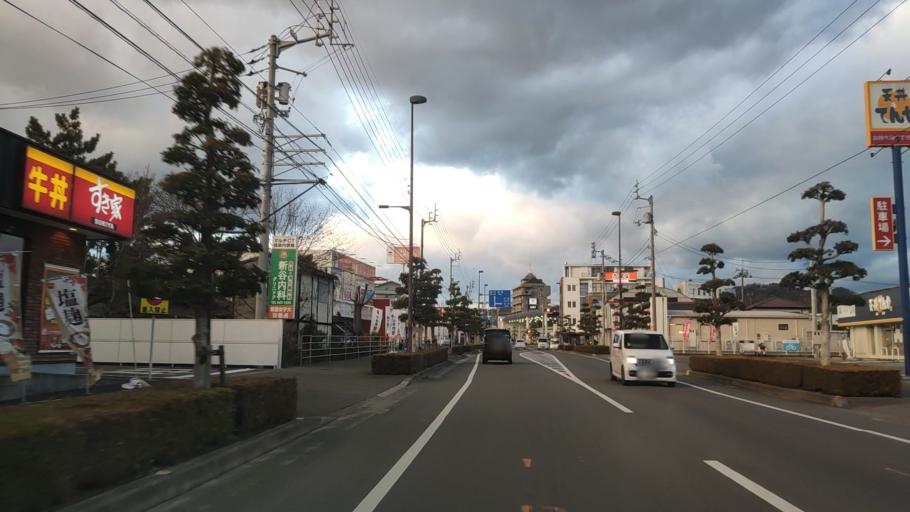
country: JP
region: Ehime
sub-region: Shikoku-chuo Shi
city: Matsuyama
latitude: 33.8361
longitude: 132.7870
